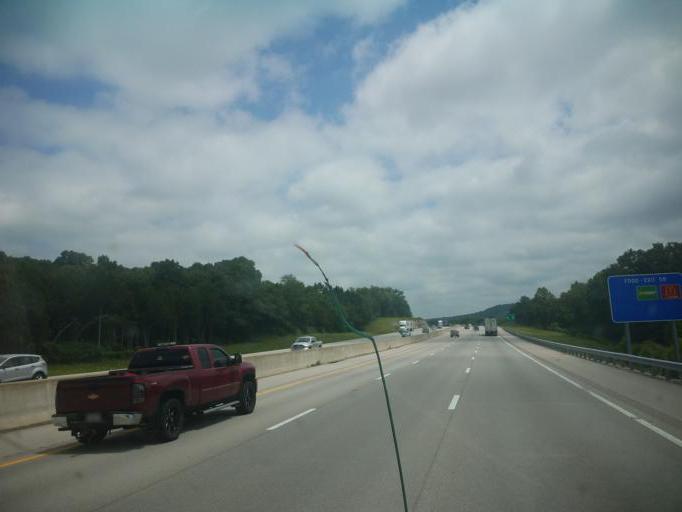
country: US
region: Kentucky
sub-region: Hart County
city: Horse Cave
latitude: 37.1871
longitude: -85.9438
